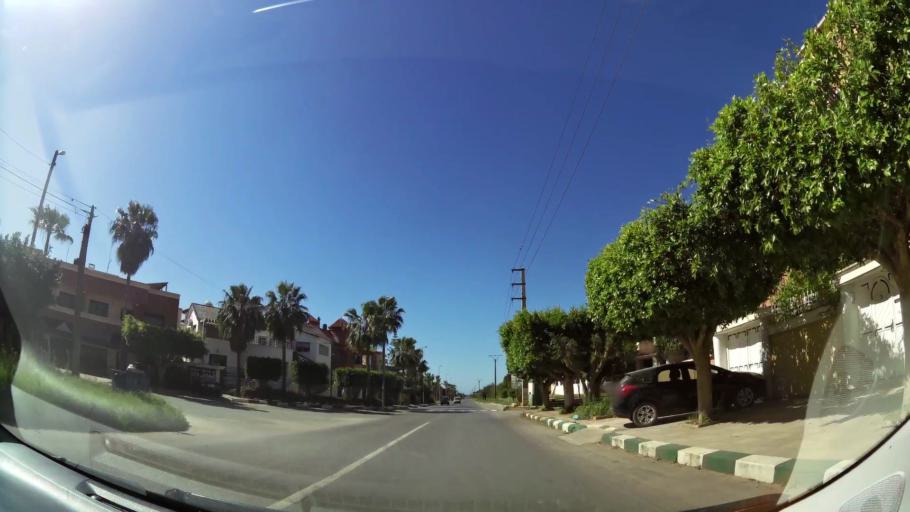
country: MA
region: Oriental
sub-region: Berkane-Taourirt
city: Berkane
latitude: 34.9398
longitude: -2.3247
